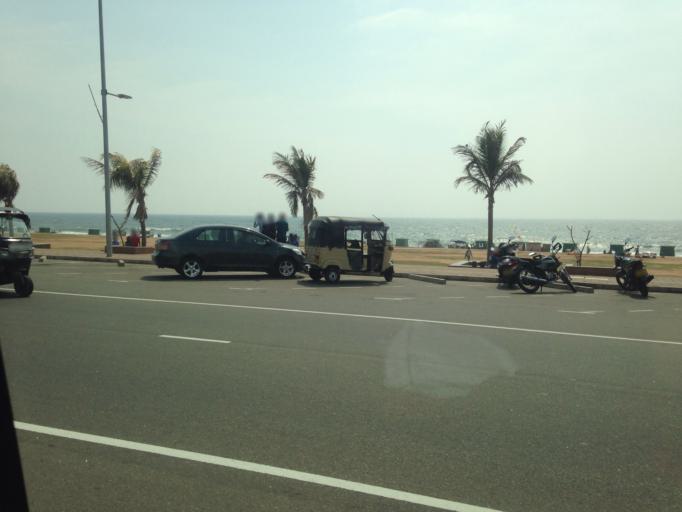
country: LK
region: Western
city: Colombo
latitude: 6.9240
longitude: 79.8454
